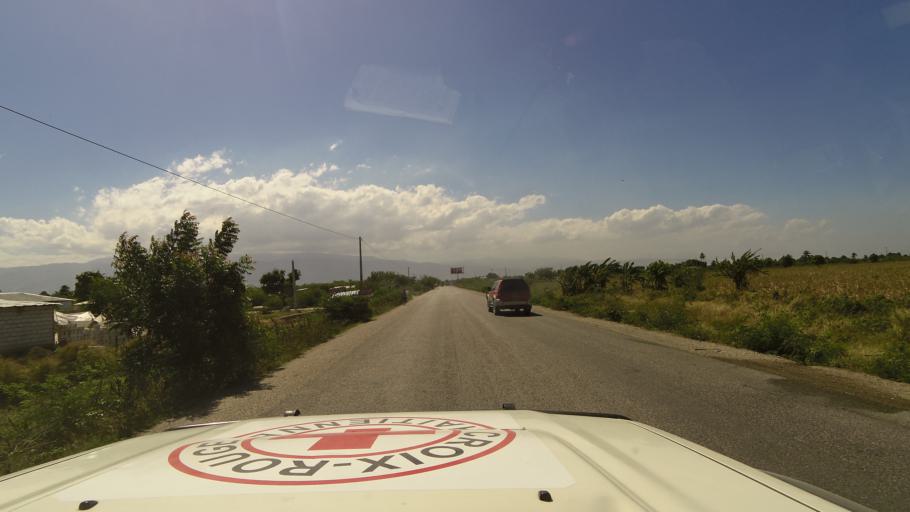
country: HT
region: Ouest
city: Delmas 73
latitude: 18.6299
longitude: -72.3073
